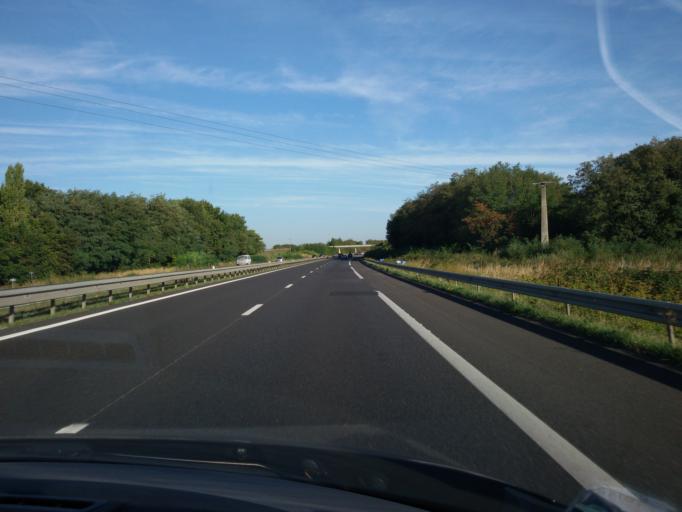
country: FR
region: Centre
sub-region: Departement du Cher
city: Mehun-sur-Yevre
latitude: 47.1088
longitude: 2.2070
